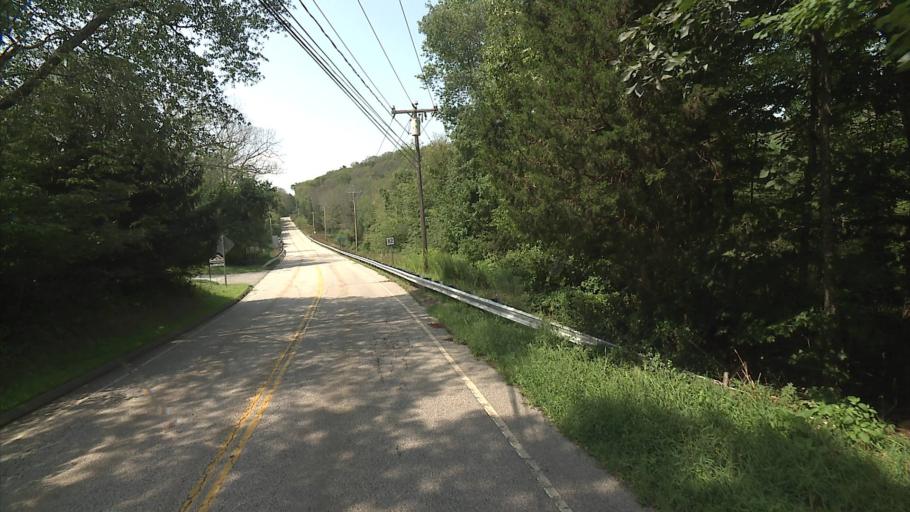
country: US
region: Connecticut
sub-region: Middlesex County
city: Deep River Center
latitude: 41.4229
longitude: -72.4002
